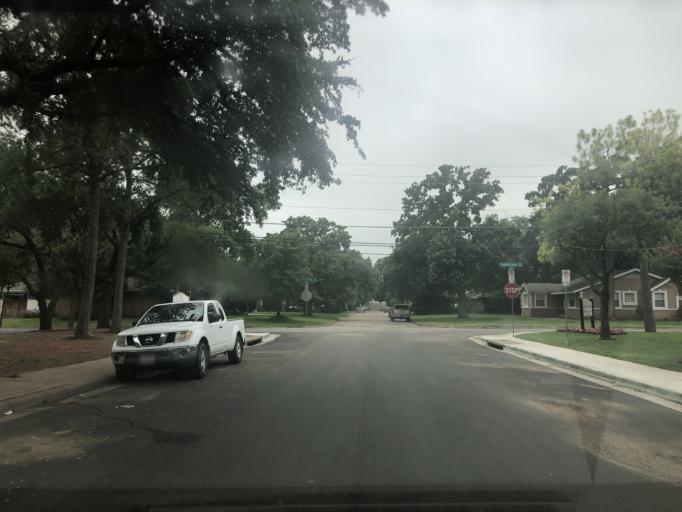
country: US
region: Texas
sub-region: Dallas County
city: University Park
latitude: 32.8587
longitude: -96.8668
